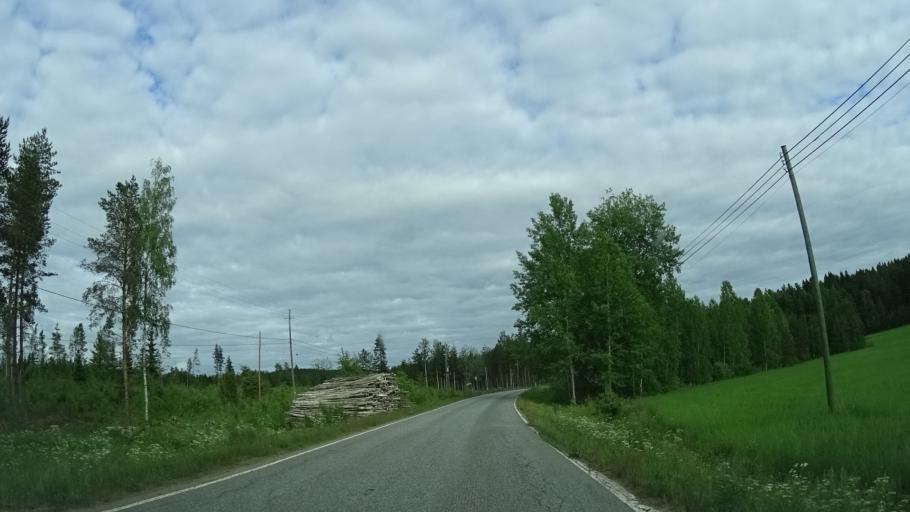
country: FI
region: Paijanne Tavastia
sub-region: Lahti
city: Sysmae
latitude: 61.6443
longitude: 25.6312
